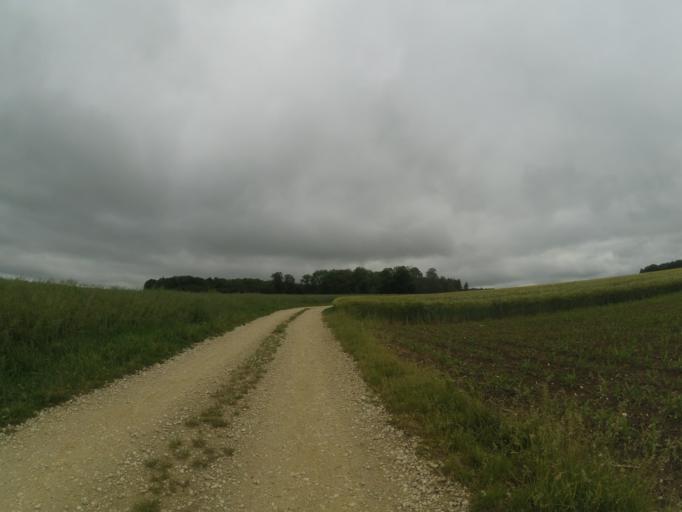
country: DE
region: Baden-Wuerttemberg
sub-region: Tuebingen Region
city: Bernstadt
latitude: 48.4578
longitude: 10.0499
